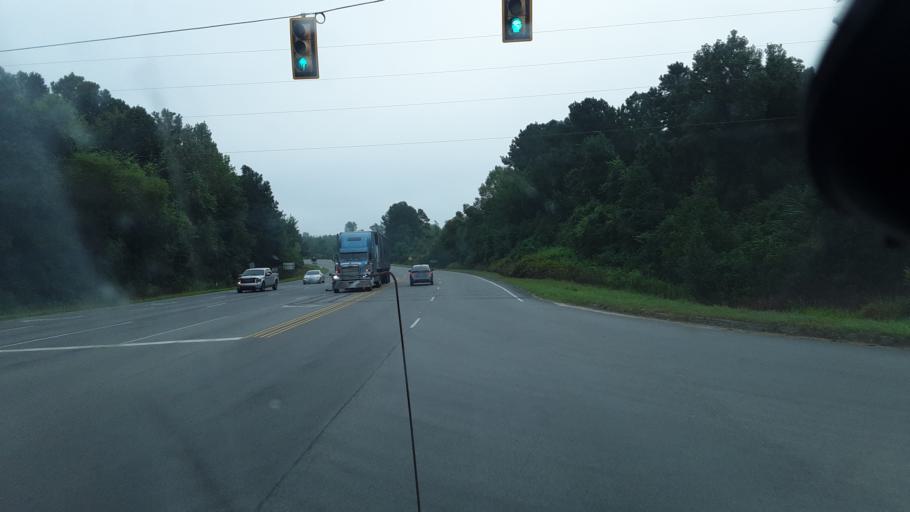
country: US
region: South Carolina
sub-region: Florence County
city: Johnsonville
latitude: 33.8827
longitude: -79.4528
